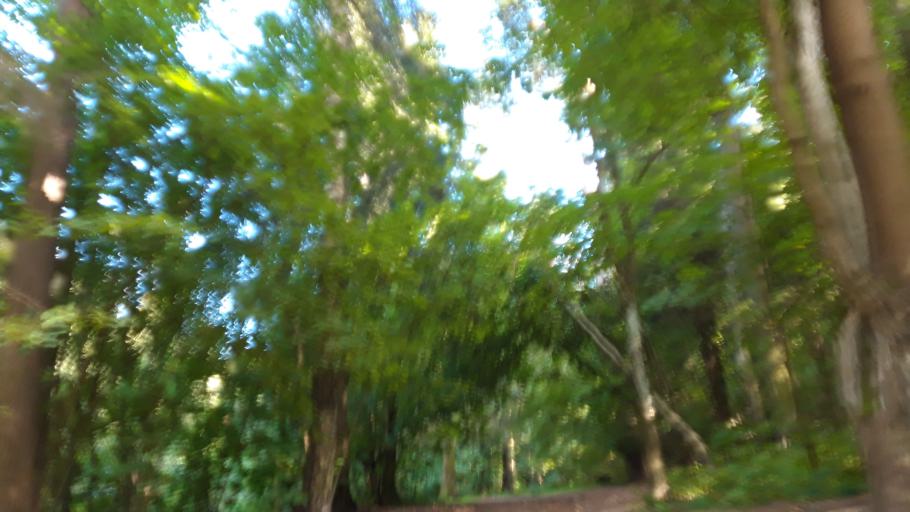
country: RU
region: Moscow
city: Zelenograd
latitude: 55.9913
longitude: 37.1919
